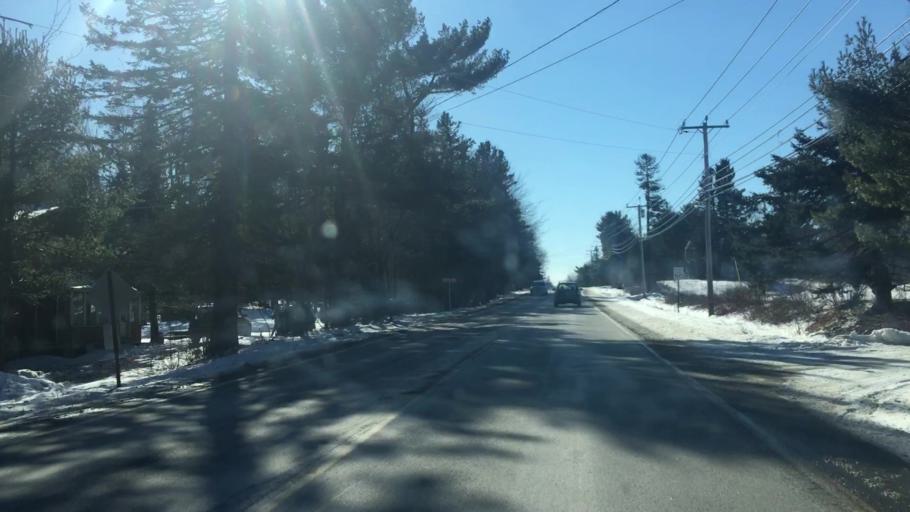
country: US
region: Maine
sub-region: Hancock County
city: Ellsworth
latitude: 44.5186
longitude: -68.4319
